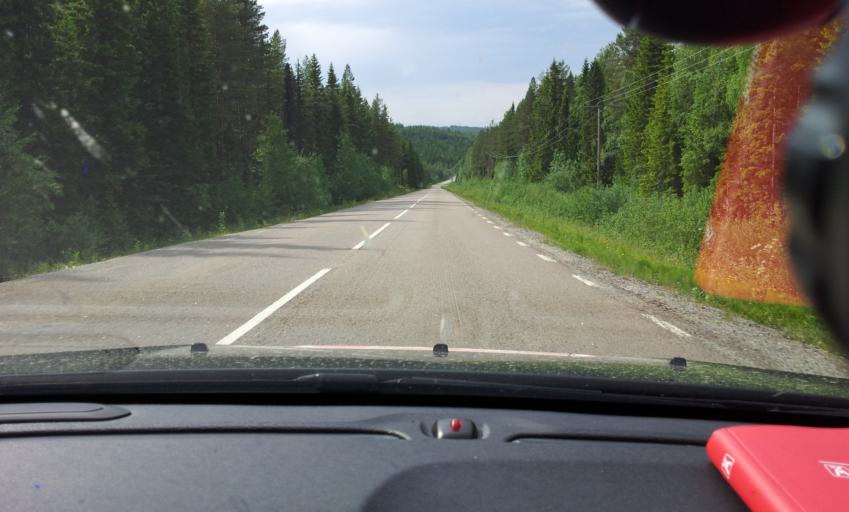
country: SE
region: Jaemtland
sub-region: OEstersunds Kommun
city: Brunflo
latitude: 62.6533
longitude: 14.8923
